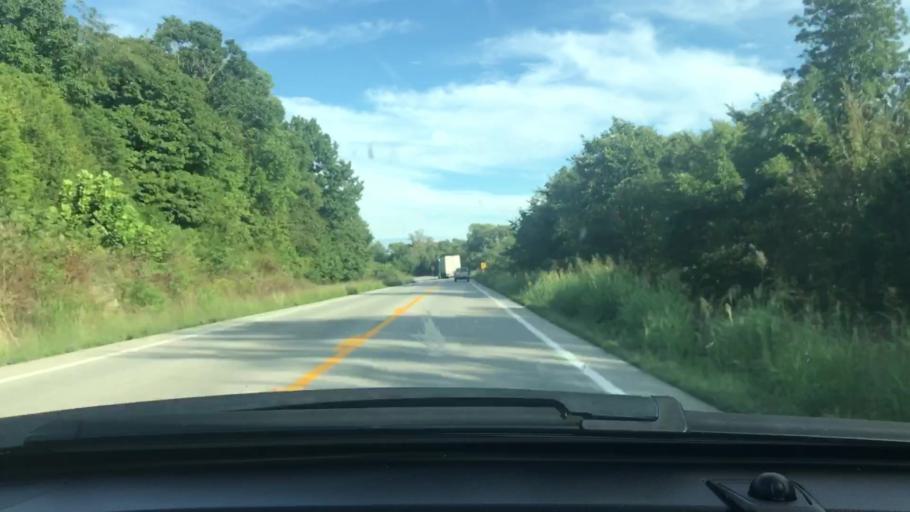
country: US
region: Arkansas
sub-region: Sharp County
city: Cherokee Village
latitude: 36.2984
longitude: -91.4384
